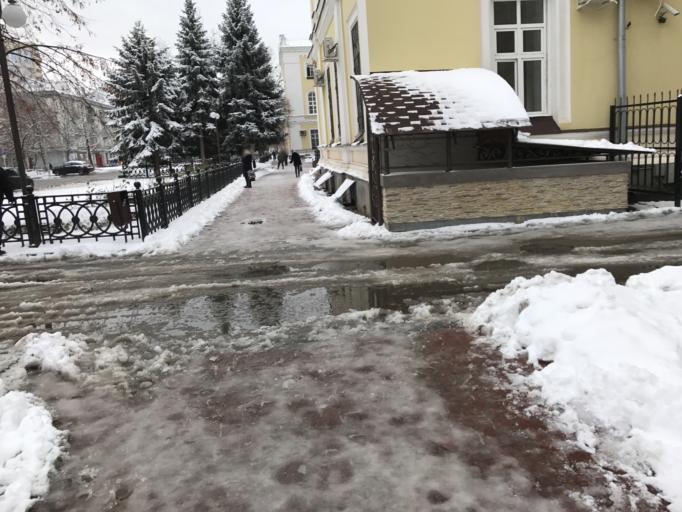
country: RU
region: Stavropol'skiy
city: Stavropol'
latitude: 45.0432
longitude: 41.9625
